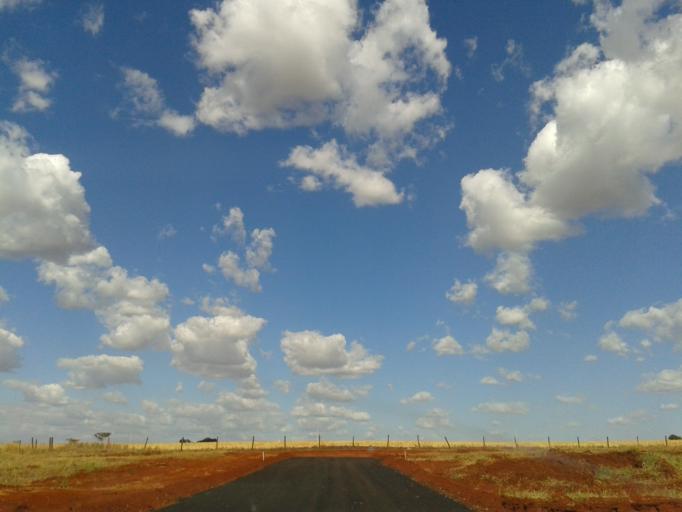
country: BR
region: Minas Gerais
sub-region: Capinopolis
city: Capinopolis
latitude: -18.6942
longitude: -49.5750
